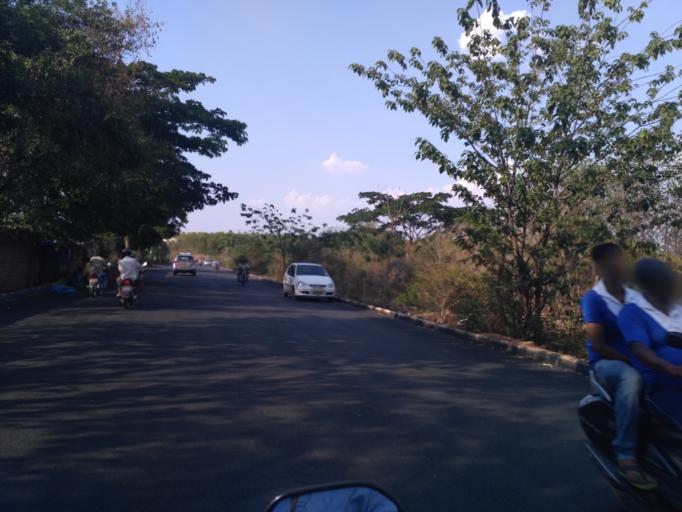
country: IN
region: Karnataka
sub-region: Bangalore Urban
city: Yelahanka
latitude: 13.0404
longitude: 77.5386
